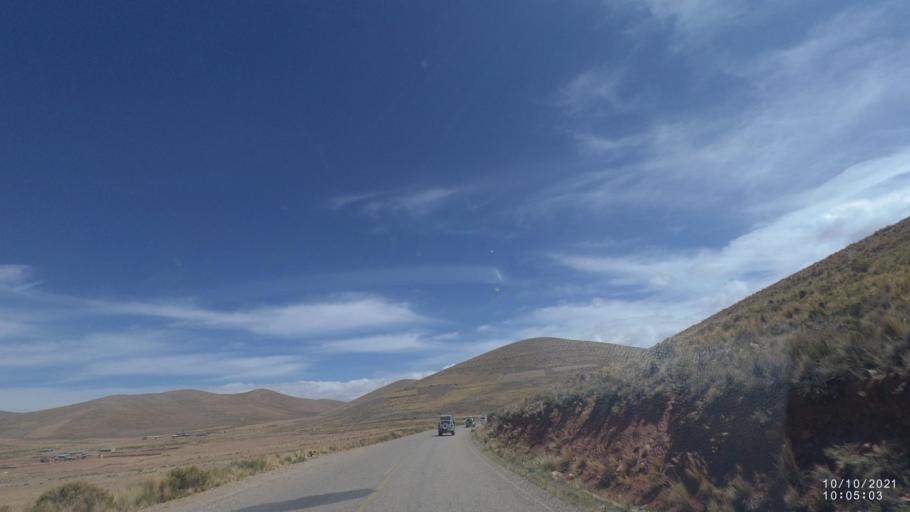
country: BO
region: La Paz
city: Eucaliptus
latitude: -17.3792
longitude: -67.4534
